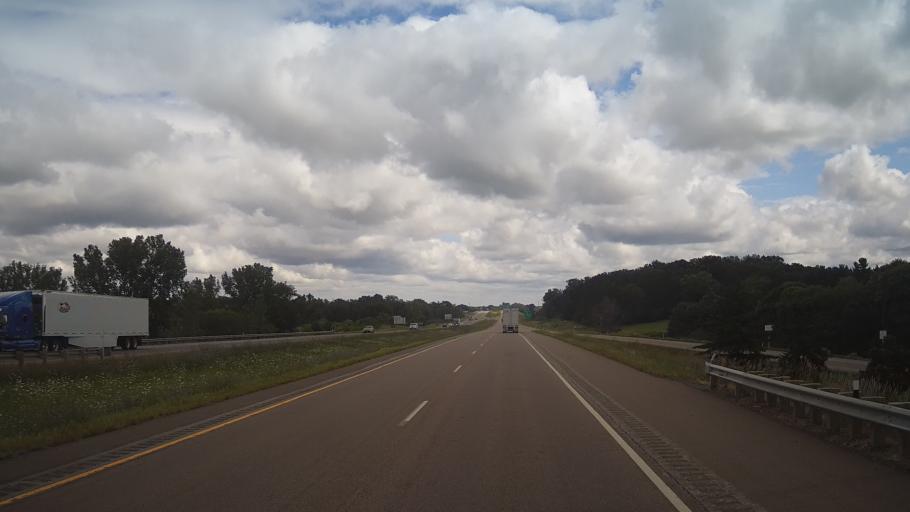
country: US
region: Wisconsin
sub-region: Monroe County
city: Tomah
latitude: 43.9731
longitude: -90.4715
